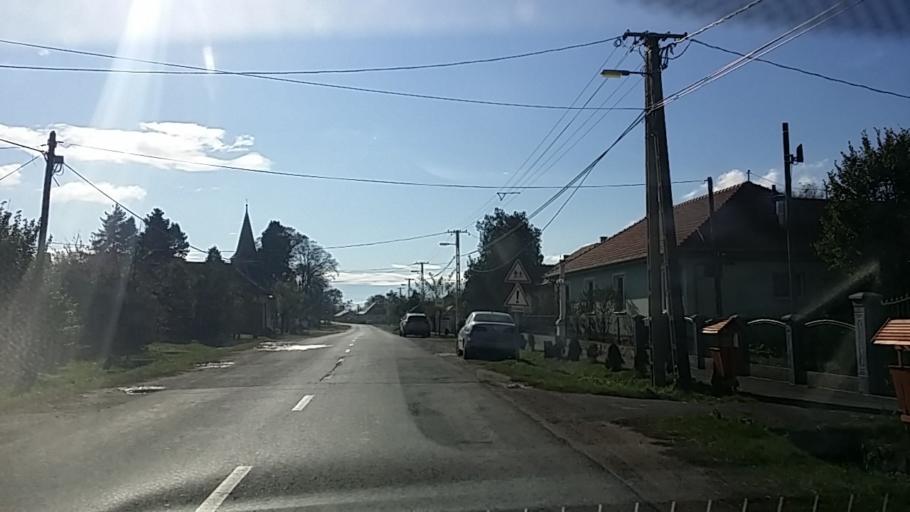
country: HU
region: Borsod-Abauj-Zemplen
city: Gonc
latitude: 48.4176
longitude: 21.2321
